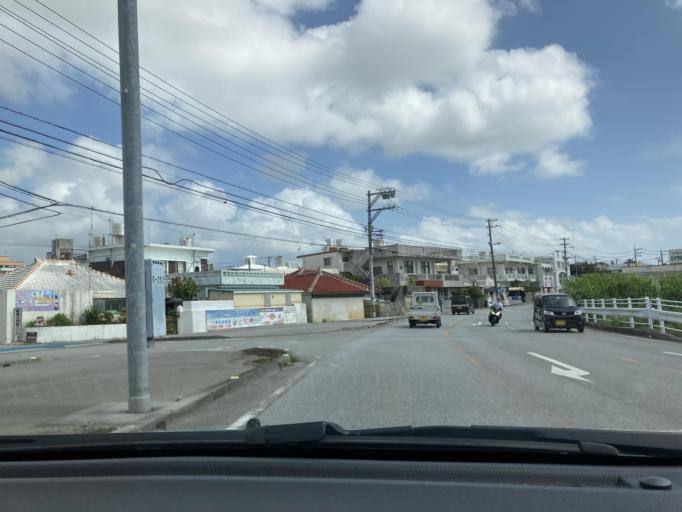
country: JP
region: Okinawa
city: Okinawa
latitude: 26.3178
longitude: 127.7997
